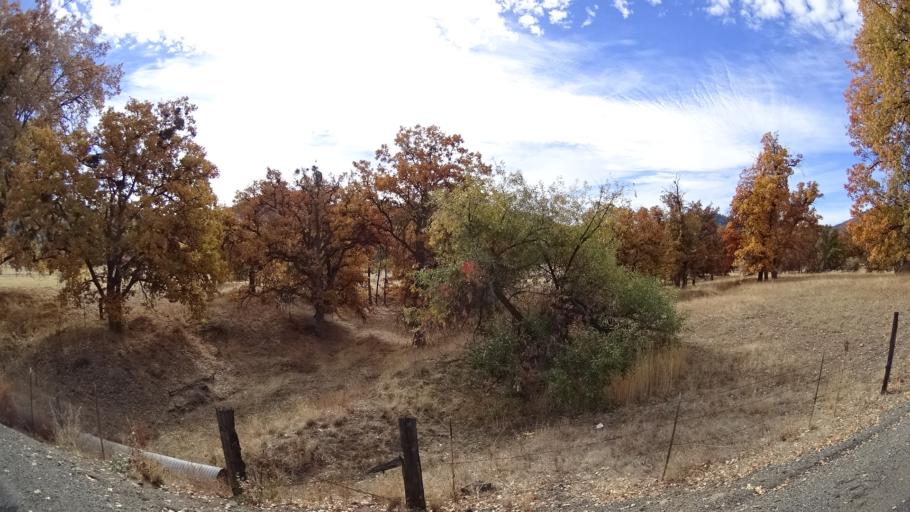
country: US
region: California
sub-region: Siskiyou County
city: Yreka
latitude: 41.6280
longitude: -122.7731
